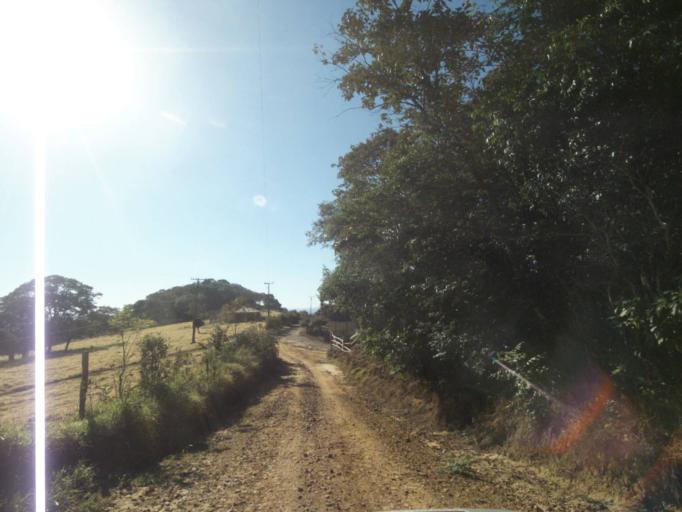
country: BR
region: Parana
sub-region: Tibagi
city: Tibagi
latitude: -24.5435
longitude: -50.4683
